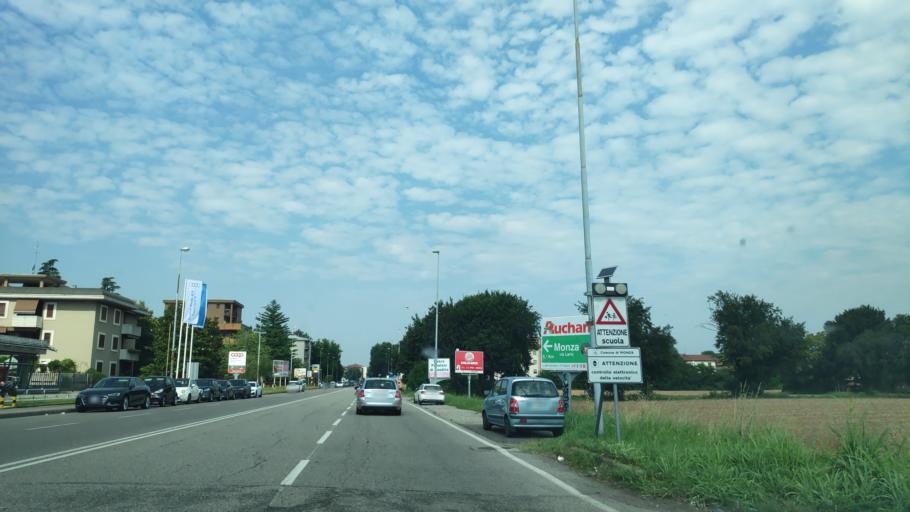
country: IT
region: Lombardy
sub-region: Provincia di Monza e Brianza
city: Villasanta
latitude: 45.5815
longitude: 9.3057
